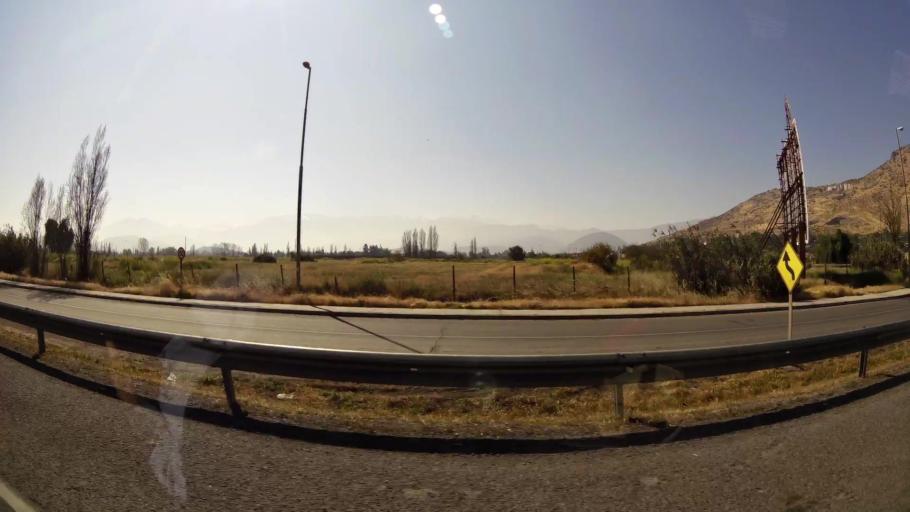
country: CL
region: Santiago Metropolitan
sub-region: Provincia de Chacabuco
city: Chicureo Abajo
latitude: -33.3031
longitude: -70.6995
